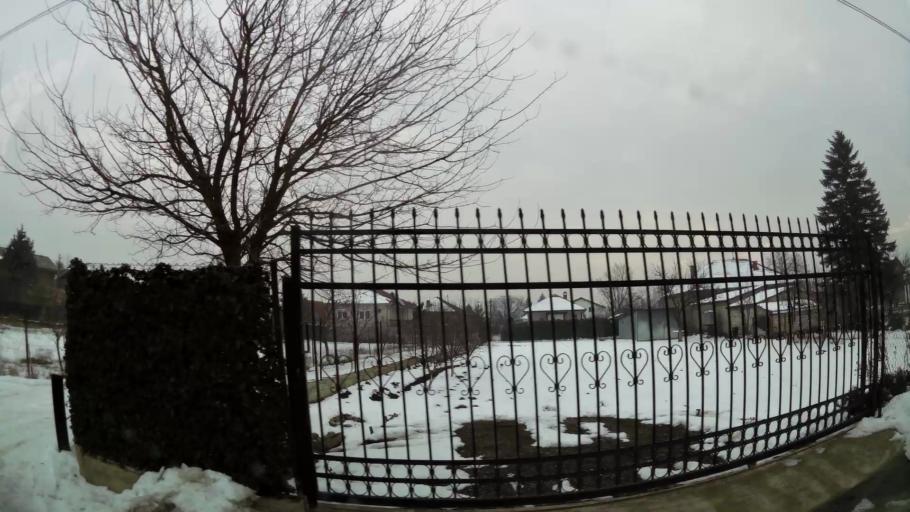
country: MK
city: Kondovo
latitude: 42.0474
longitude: 21.3543
